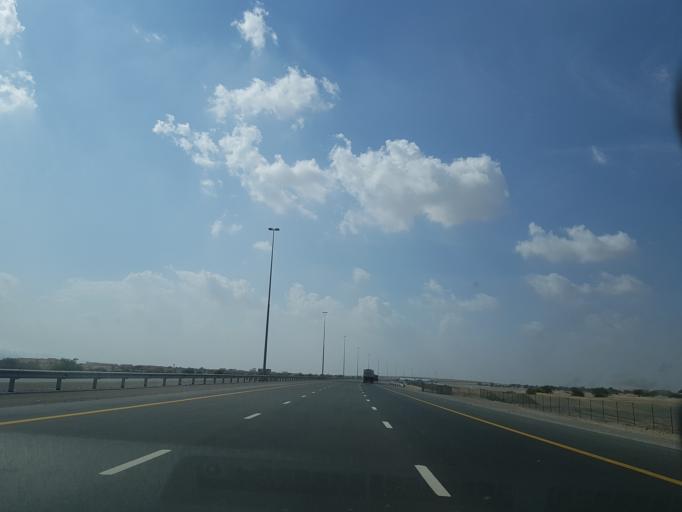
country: AE
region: Ra's al Khaymah
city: Ras al-Khaimah
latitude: 25.7268
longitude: 56.0125
